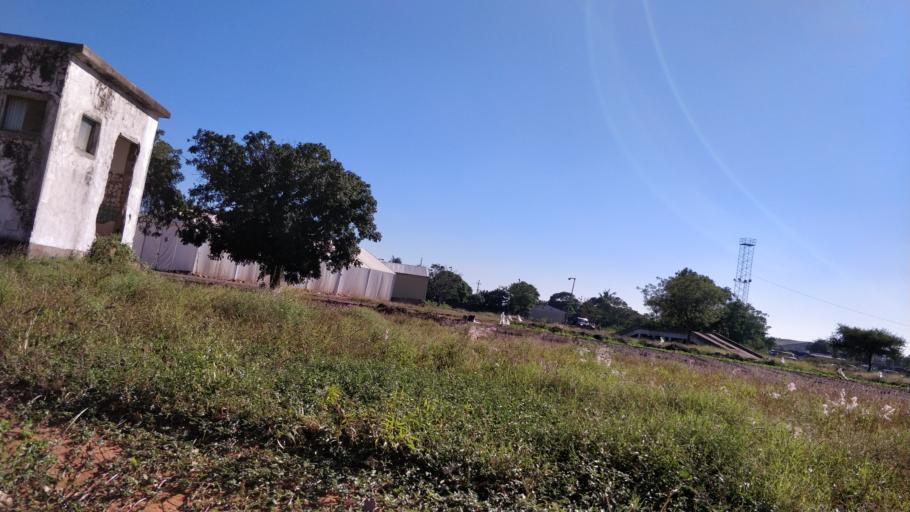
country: MZ
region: Maputo City
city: Maputo
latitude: -25.9313
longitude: 32.5997
